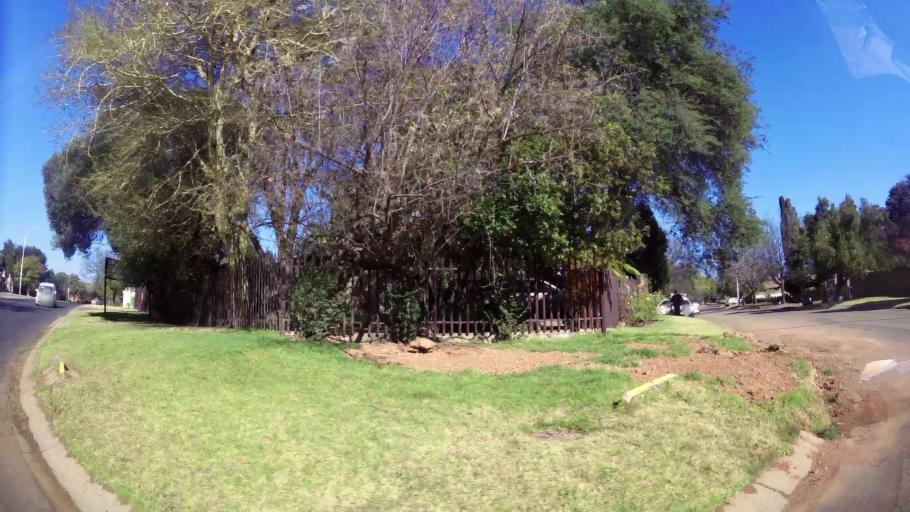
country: ZA
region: Mpumalanga
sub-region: Nkangala District Municipality
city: Witbank
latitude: -25.8718
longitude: 29.2509
